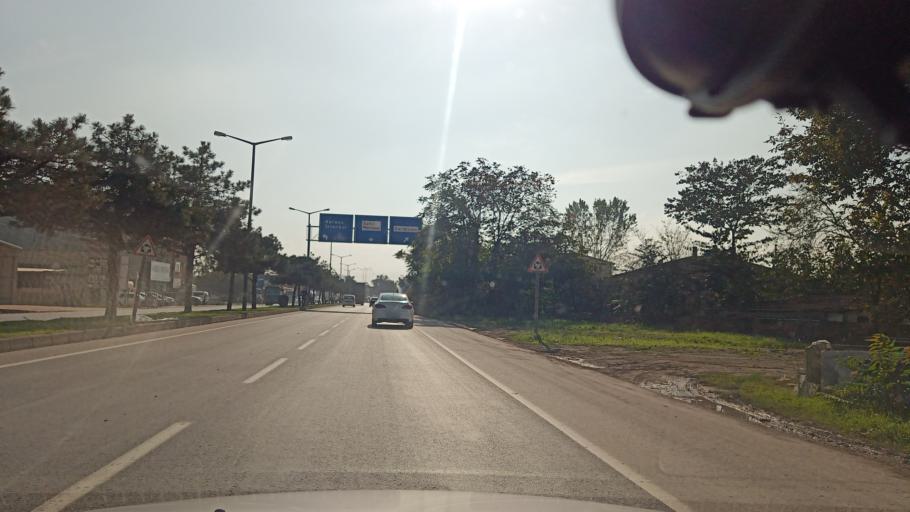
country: TR
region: Sakarya
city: Adapazari
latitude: 40.8031
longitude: 30.4060
